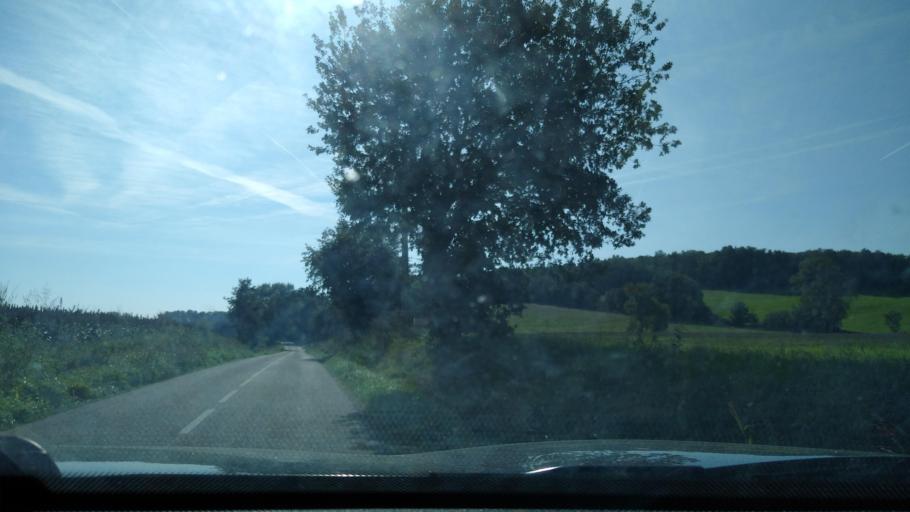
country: FR
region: Midi-Pyrenees
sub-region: Departement de la Haute-Garonne
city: Montaigut-sur-Save
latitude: 43.7362
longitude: 1.2426
